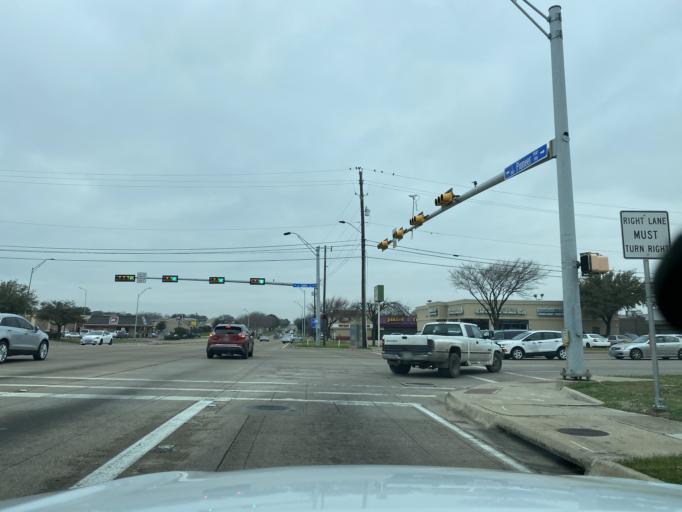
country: US
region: Texas
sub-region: Tarrant County
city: Arlington
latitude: 32.7082
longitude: -97.0973
